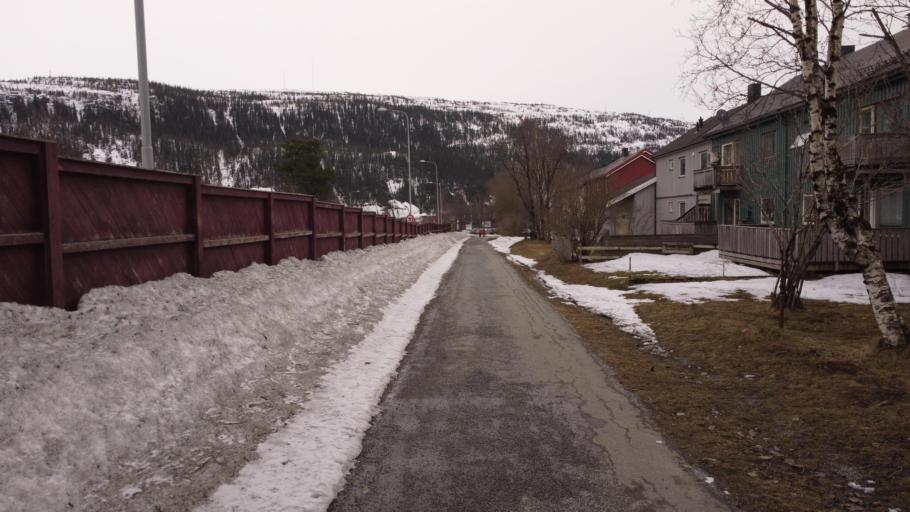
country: NO
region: Nordland
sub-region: Rana
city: Mo i Rana
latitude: 66.3125
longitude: 14.1549
